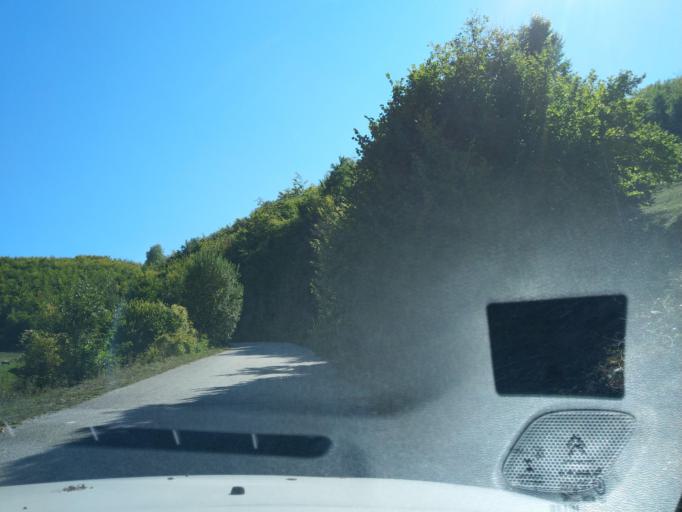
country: RS
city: Sokolovica
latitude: 43.2573
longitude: 20.3021
